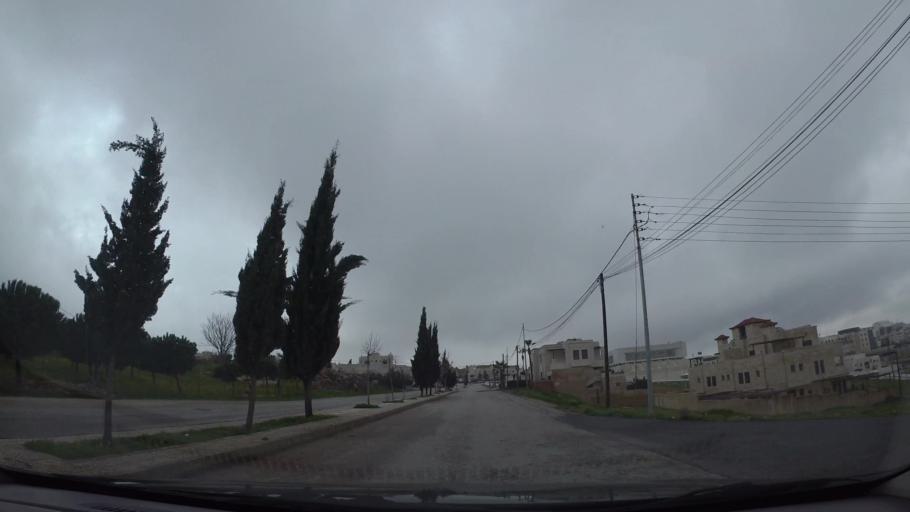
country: JO
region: Amman
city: Al Bunayyat ash Shamaliyah
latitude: 31.9368
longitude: 35.8906
